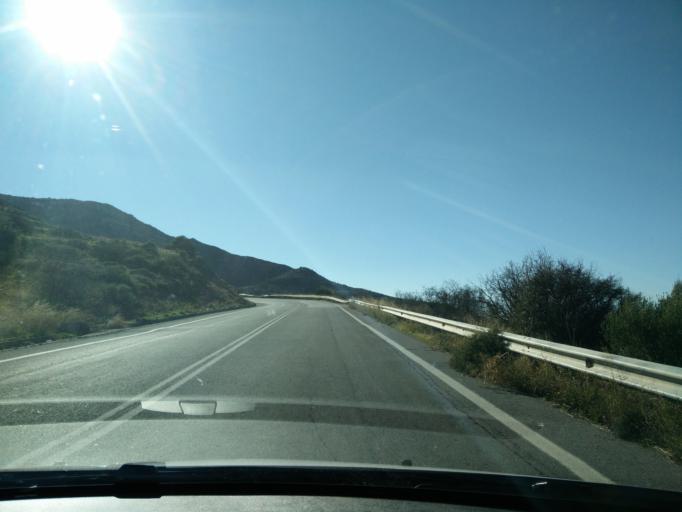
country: GR
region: Crete
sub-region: Nomos Irakleiou
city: Arkalochori
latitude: 35.0687
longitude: 25.3555
